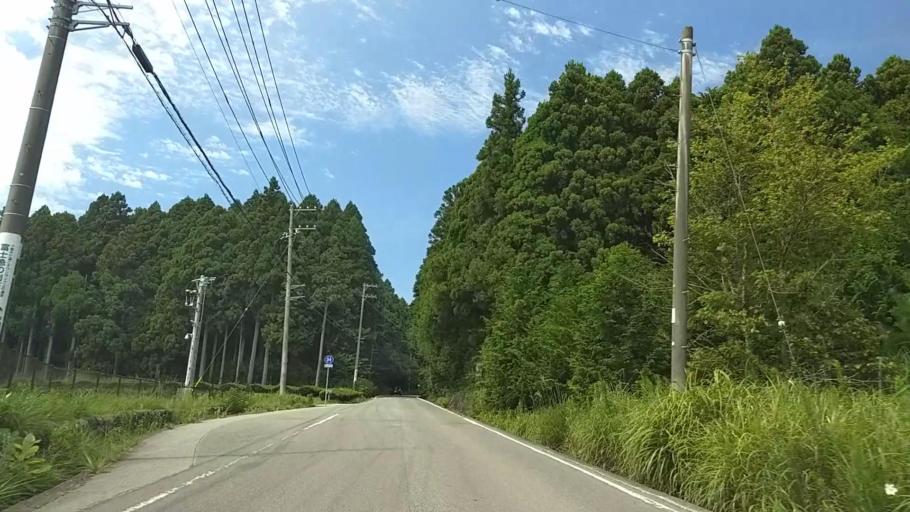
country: JP
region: Shizuoka
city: Gotemba
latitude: 35.2429
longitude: 138.8659
